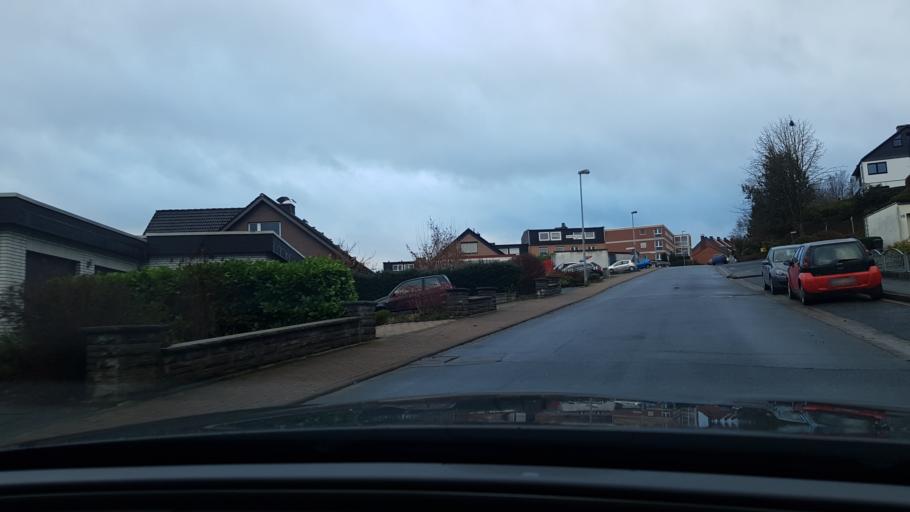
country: DE
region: Lower Saxony
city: Hardegsen
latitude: 51.6495
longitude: 9.8197
